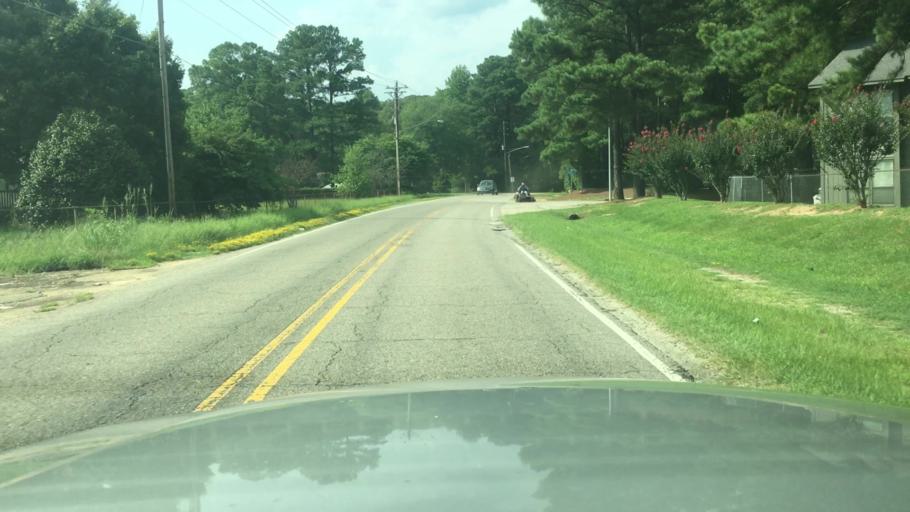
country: US
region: North Carolina
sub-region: Cumberland County
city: Fayetteville
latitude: 35.0908
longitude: -78.9427
